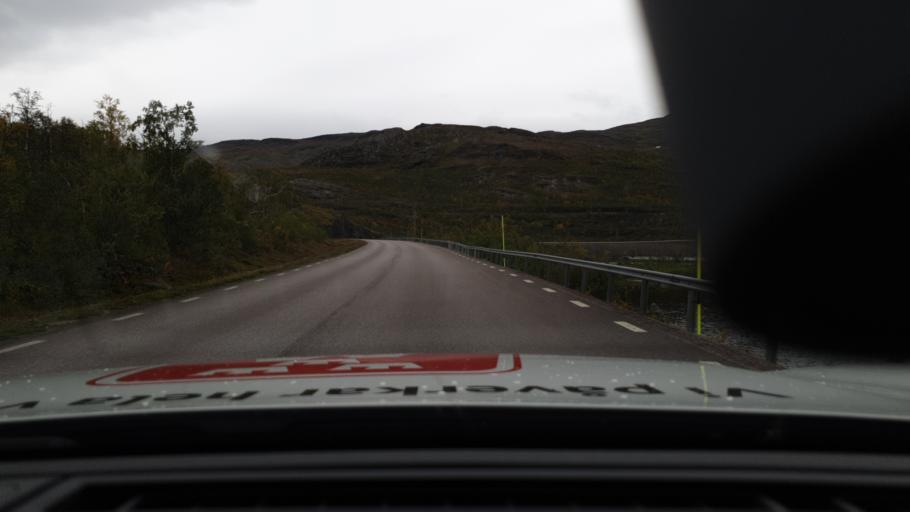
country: NO
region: Troms
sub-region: Bardu
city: Setermoen
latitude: 68.4389
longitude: 18.5877
